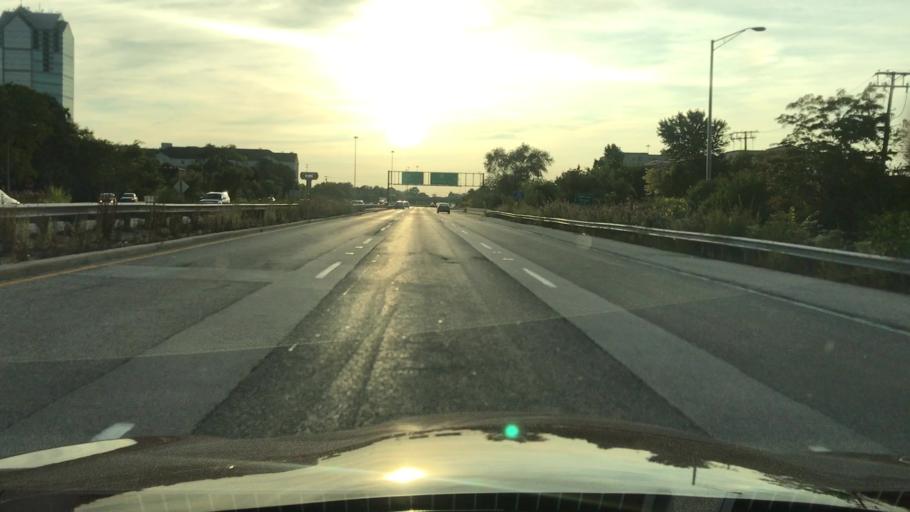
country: US
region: Illinois
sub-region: DuPage County
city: Oakbrook Terrace
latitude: 41.8611
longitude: -87.9467
